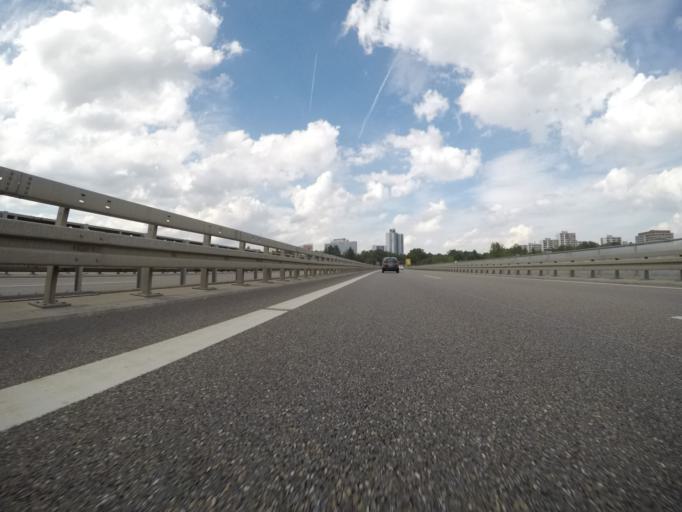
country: DE
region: Baden-Wuerttemberg
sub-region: Regierungsbezirk Stuttgart
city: Leinfelden-Echterdingen
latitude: 48.7168
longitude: 9.1631
